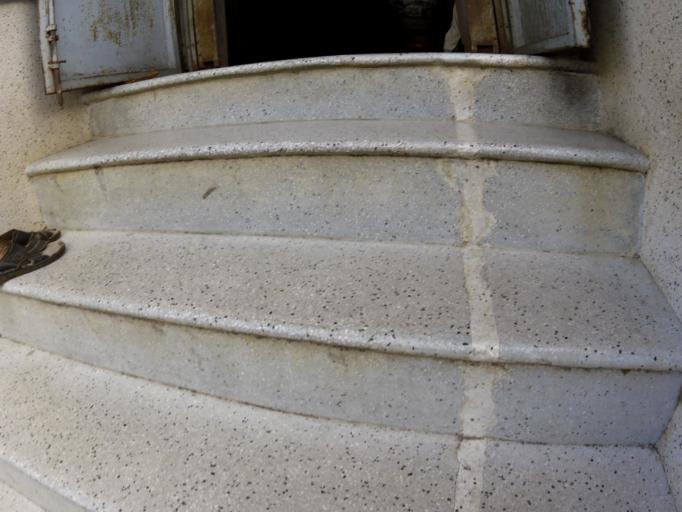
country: VN
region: Khanh Hoa
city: Nha Trang
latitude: 12.2521
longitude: 109.1809
